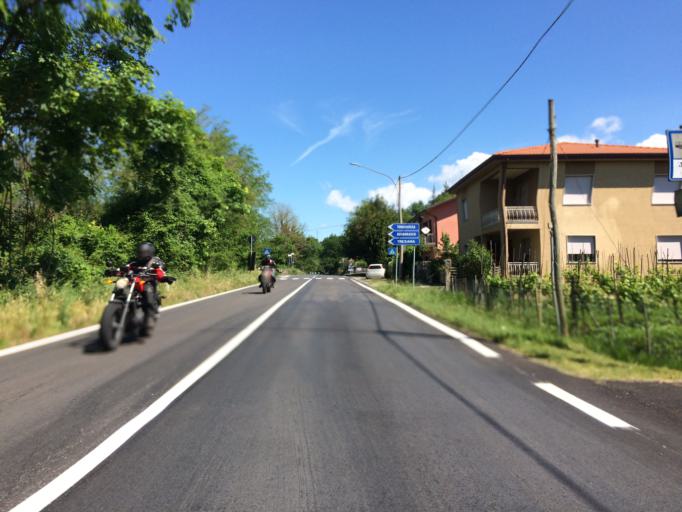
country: IT
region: Tuscany
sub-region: Provincia di Massa-Carrara
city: Terrarossa
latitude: 44.2412
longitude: 9.9595
